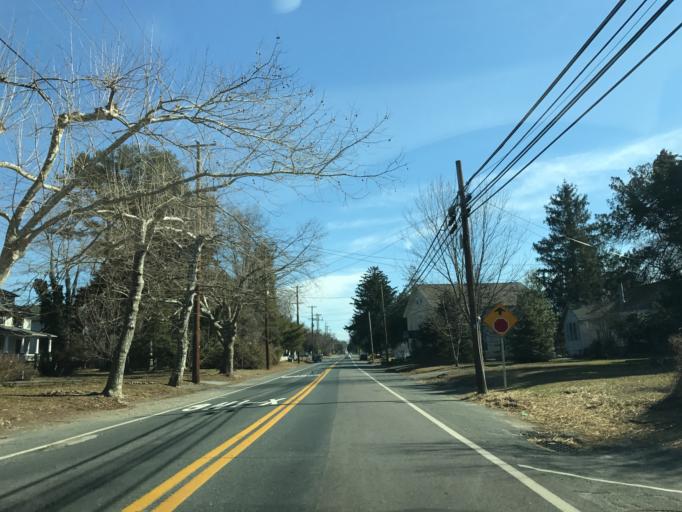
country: US
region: Maryland
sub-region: Cecil County
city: North East
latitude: 39.6014
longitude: -75.9388
